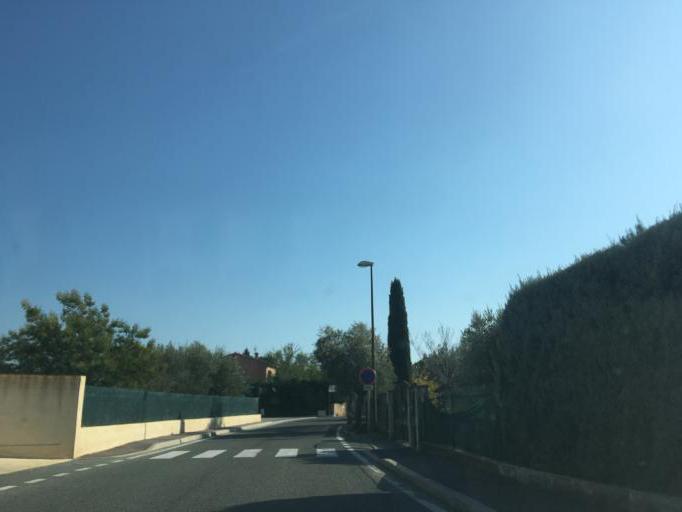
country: FR
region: Provence-Alpes-Cote d'Azur
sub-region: Departement du Var
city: Figanieres
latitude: 43.5711
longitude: 6.4990
